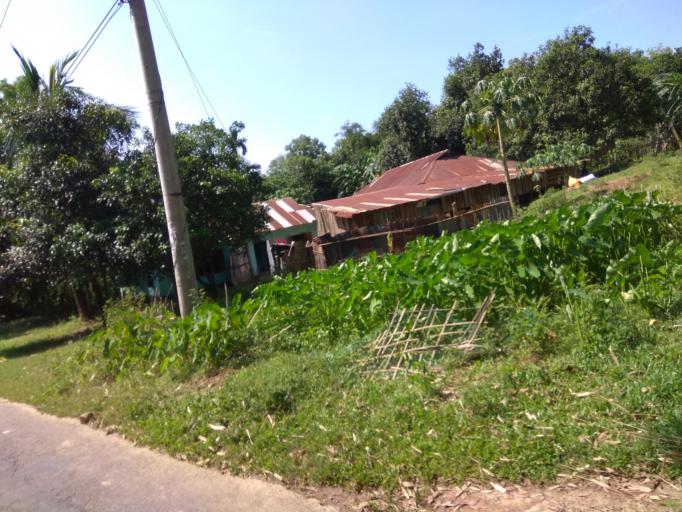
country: BD
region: Chittagong
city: Khagrachhari
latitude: 23.0314
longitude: 92.0109
